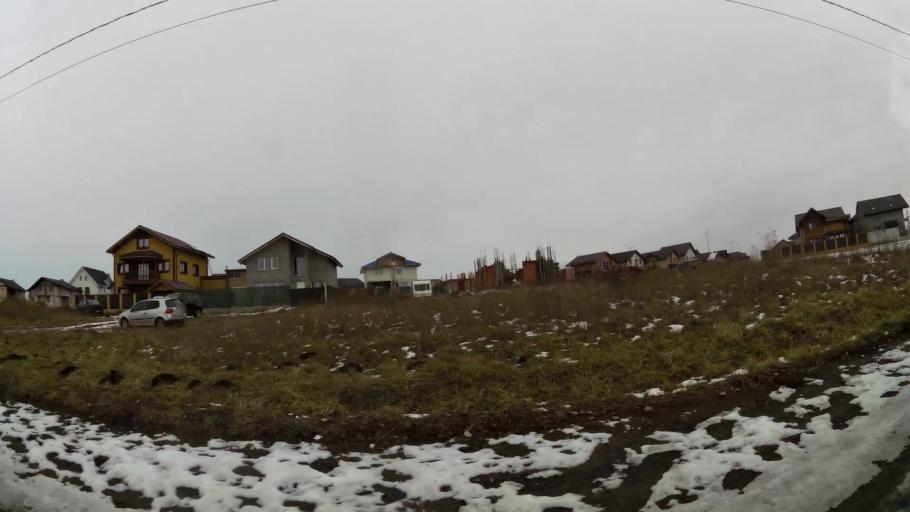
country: RO
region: Ilfov
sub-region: Comuna Tunari
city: Tunari
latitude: 44.5528
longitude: 26.1513
